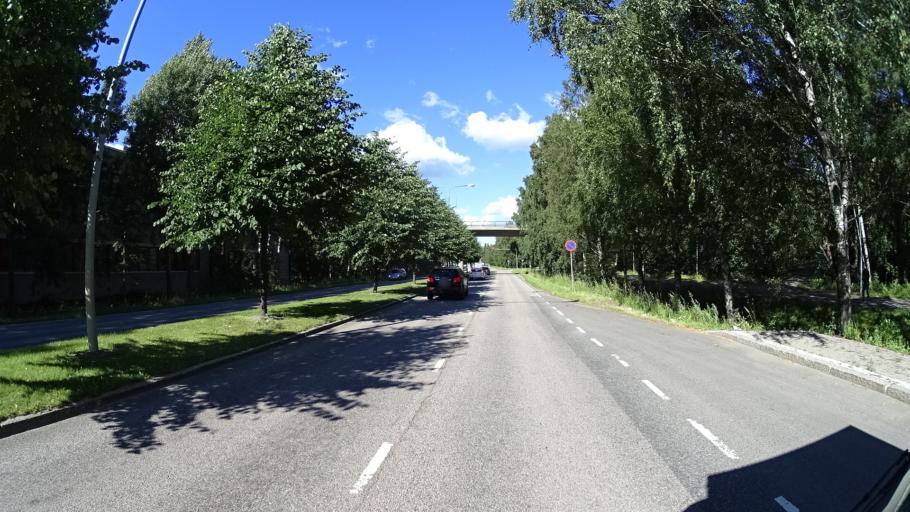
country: FI
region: Uusimaa
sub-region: Helsinki
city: Vantaa
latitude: 60.2309
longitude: 25.0788
